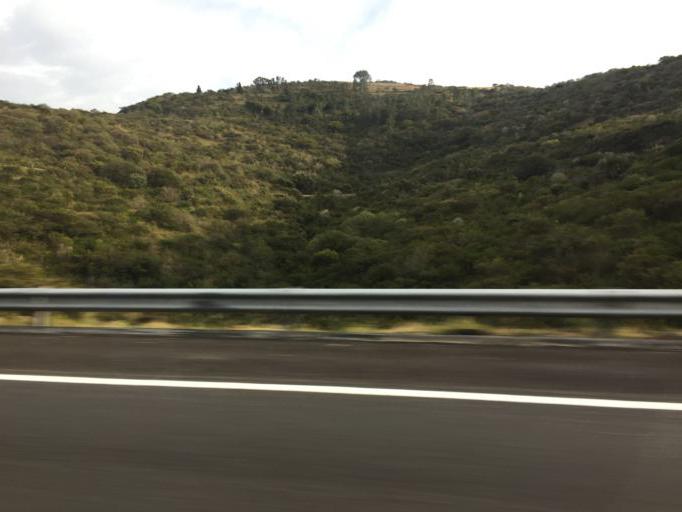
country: MX
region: Michoacan
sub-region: Cuitzeo
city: San Juan Benito Juarez (San Juan Tararameo)
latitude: 19.8935
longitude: -101.1573
